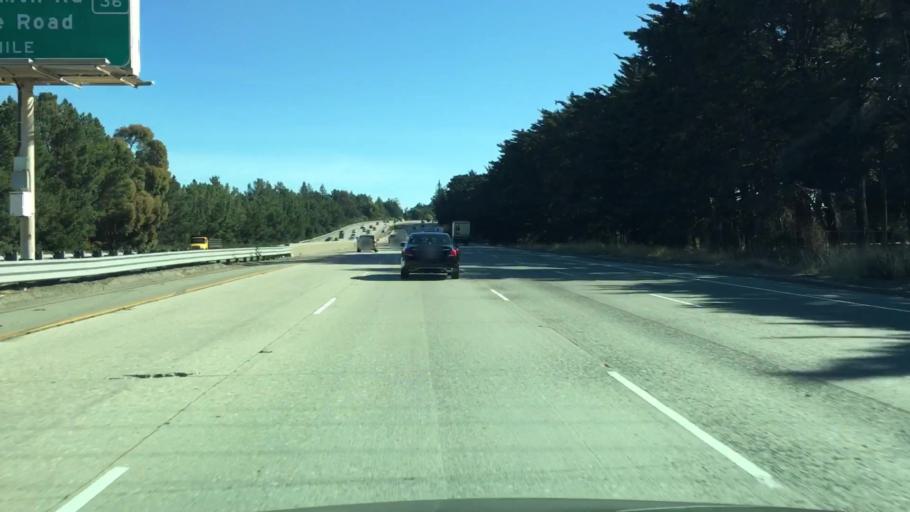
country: US
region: California
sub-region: San Mateo County
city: Hillsborough
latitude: 37.5624
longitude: -122.3855
